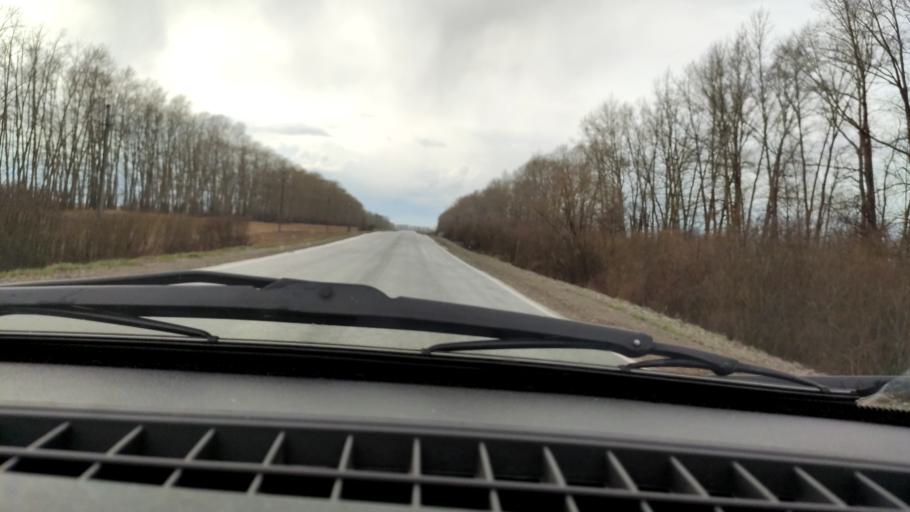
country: RU
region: Bashkortostan
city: Alekseyevka
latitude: 55.0595
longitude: 55.1092
